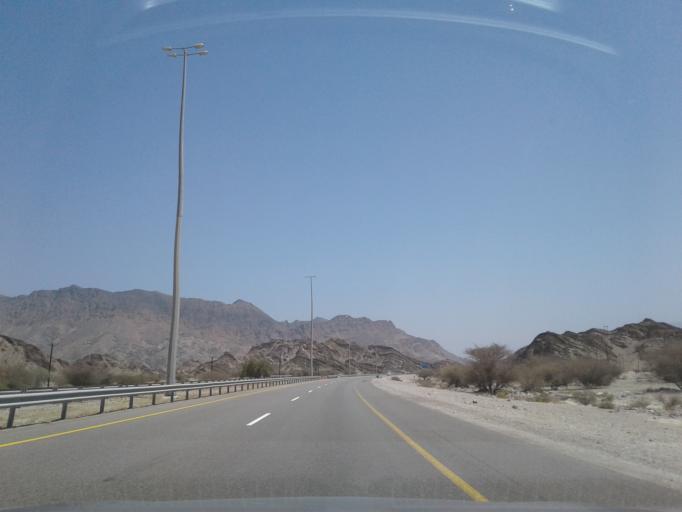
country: OM
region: Muhafazat Masqat
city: Muscat
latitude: 23.3315
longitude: 58.7110
